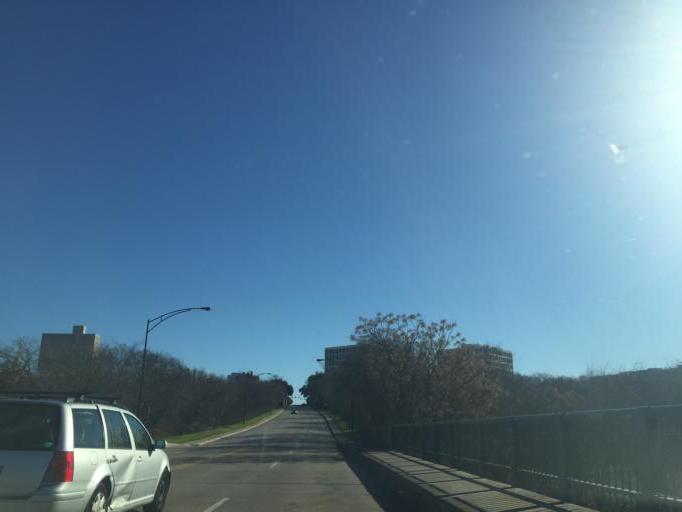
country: US
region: Texas
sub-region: Tarrant County
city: Fort Worth
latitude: 32.7467
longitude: -97.3466
